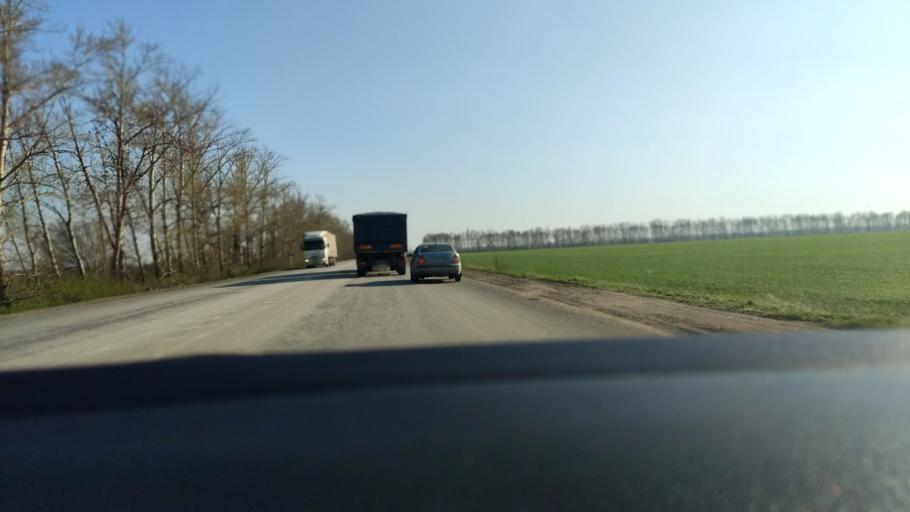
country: RU
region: Voronezj
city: Maslovka
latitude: 51.4428
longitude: 39.3028
